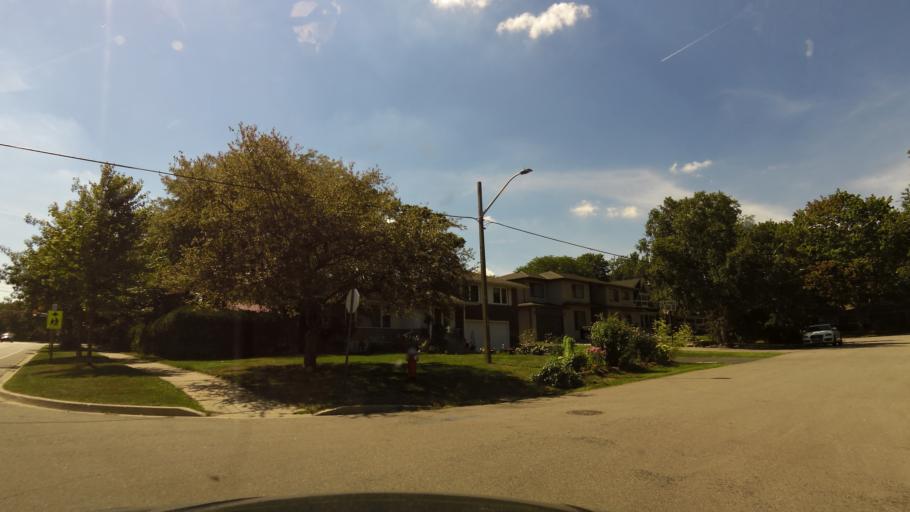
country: CA
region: Ontario
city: Mississauga
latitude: 43.5268
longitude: -79.6349
